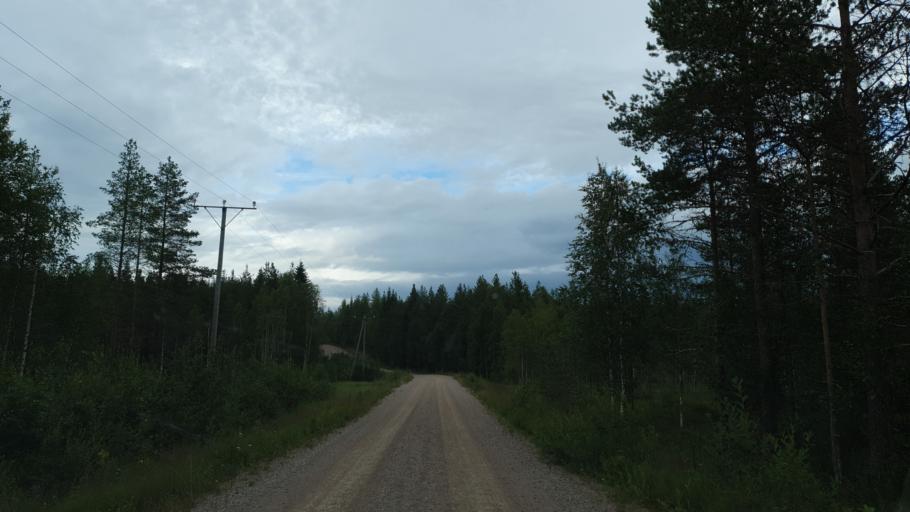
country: FI
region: Kainuu
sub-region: Kehys-Kainuu
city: Suomussalmi
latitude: 64.4516
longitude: 28.9732
